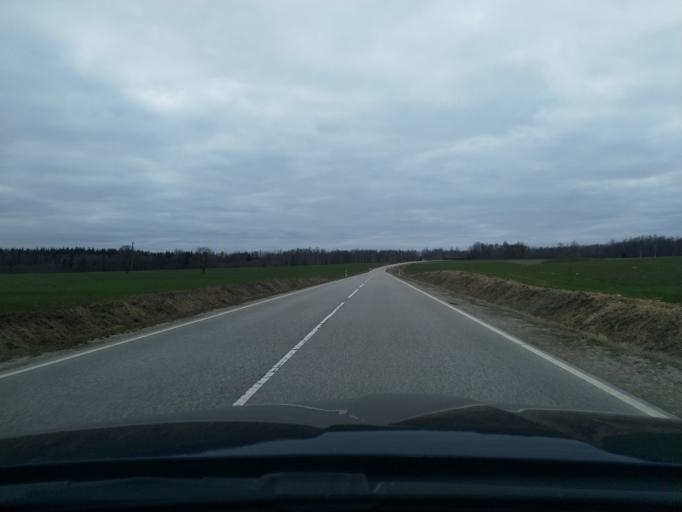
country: LV
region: Talsu Rajons
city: Sabile
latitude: 56.9427
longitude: 22.4881
